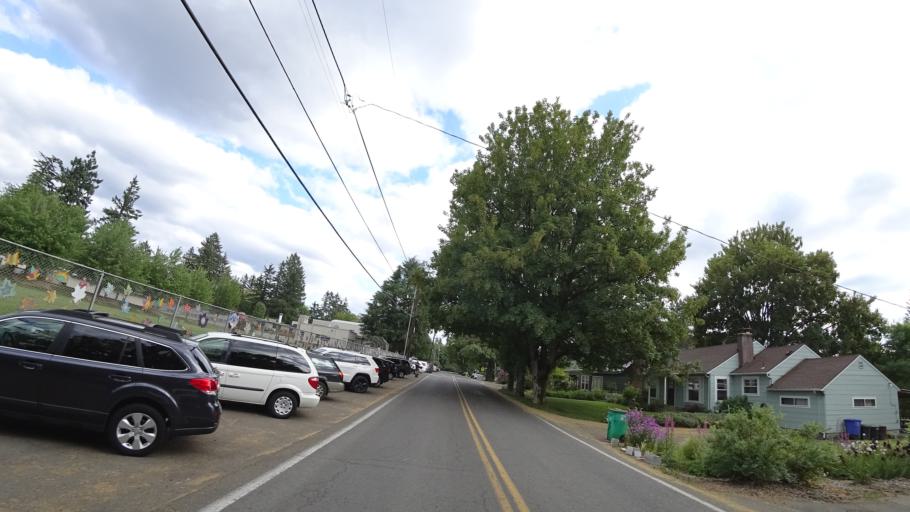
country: US
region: Oregon
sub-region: Washington County
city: Garden Home-Whitford
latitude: 45.4718
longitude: -122.7306
